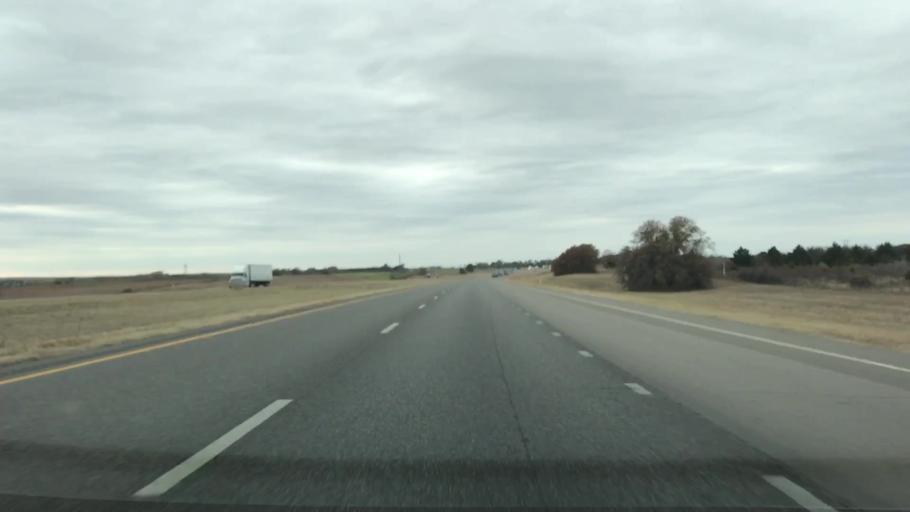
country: US
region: Oklahoma
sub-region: Beckham County
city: Erick
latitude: 35.2267
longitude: -99.9164
